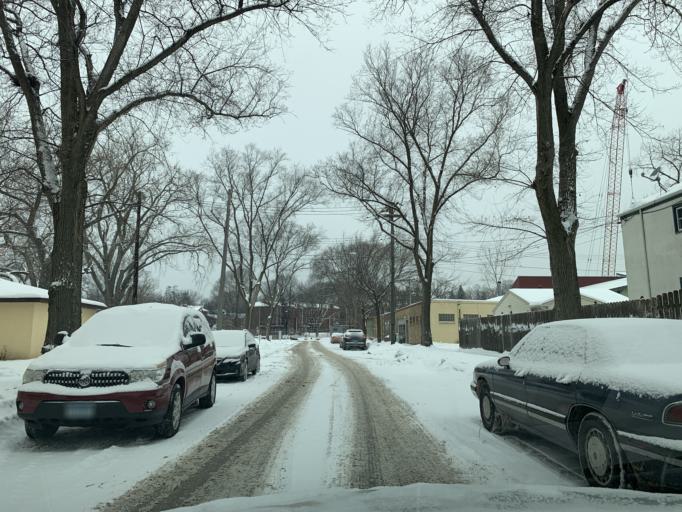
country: US
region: Minnesota
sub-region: Hennepin County
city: Saint Louis Park
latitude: 44.9520
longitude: -93.3189
